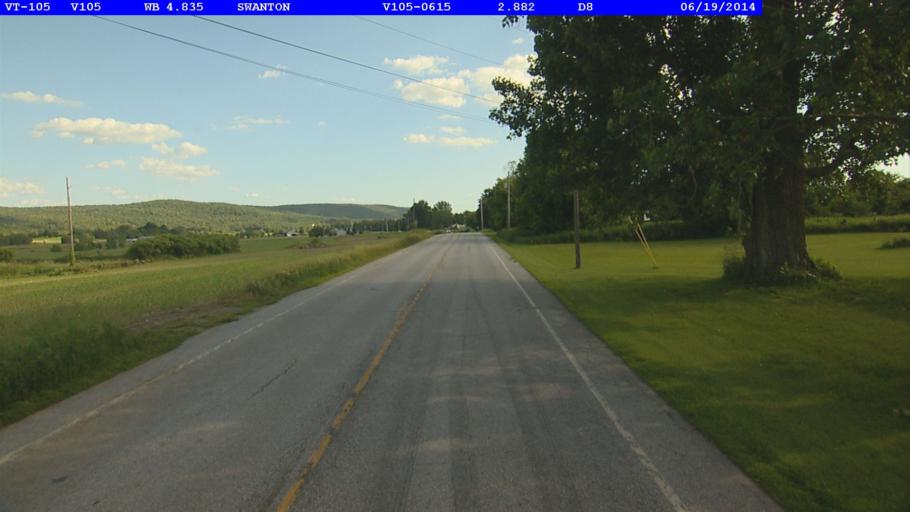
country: US
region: Vermont
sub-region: Franklin County
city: Saint Albans
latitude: 44.8739
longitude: -73.0316
